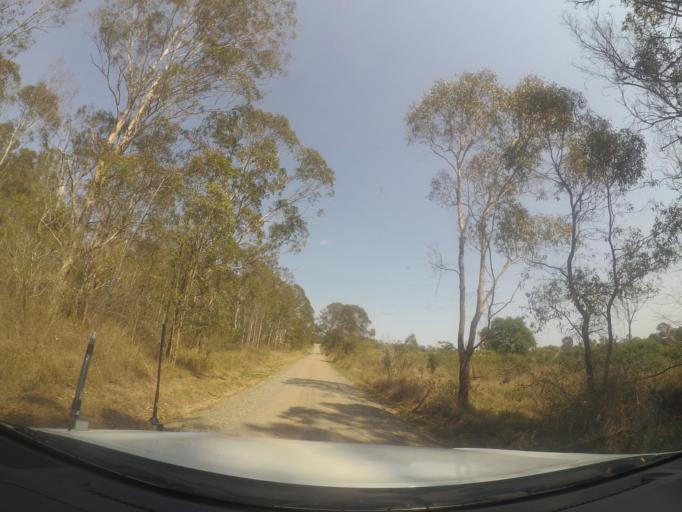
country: AU
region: Queensland
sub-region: Logan
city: North Maclean
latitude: -27.7689
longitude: 153.0383
